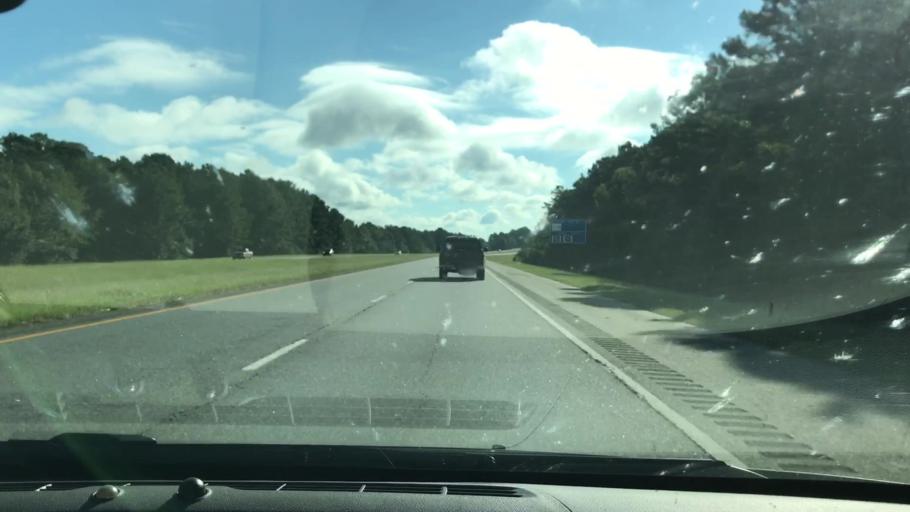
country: US
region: Georgia
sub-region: Dougherty County
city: Albany
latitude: 31.6154
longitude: -84.1906
